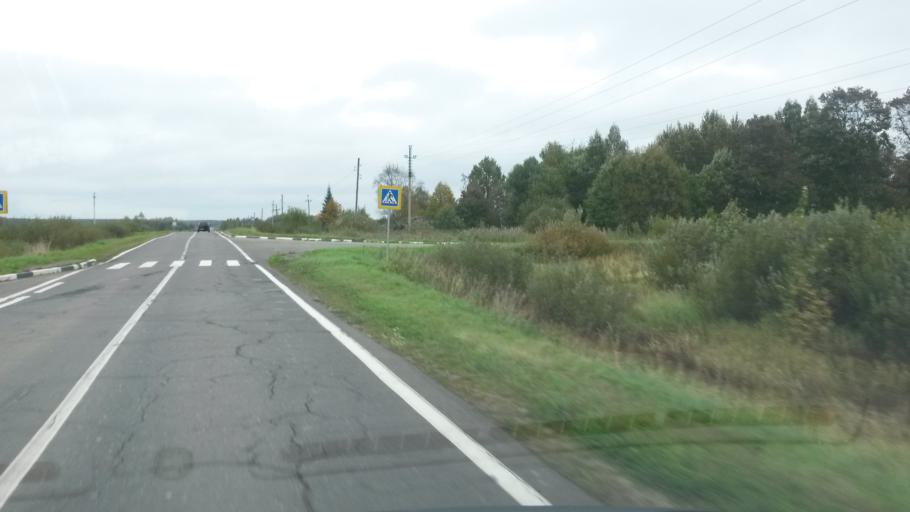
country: RU
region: Jaroslavl
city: Tutayev
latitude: 57.9501
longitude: 39.4448
